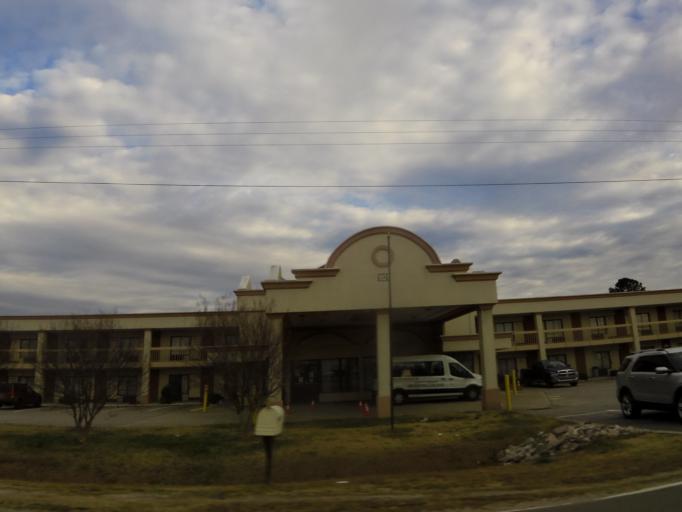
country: US
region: North Carolina
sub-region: Nash County
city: Rocky Mount
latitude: 35.9864
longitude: -77.7833
